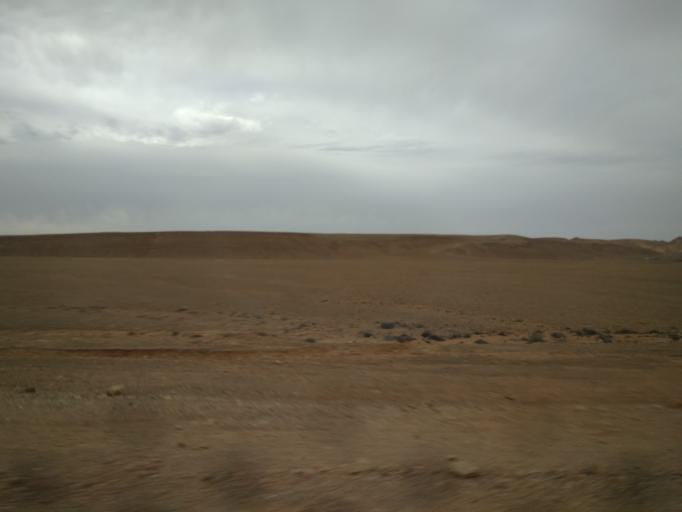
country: IL
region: Southern District
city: Eilat
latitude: 29.8539
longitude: 34.8424
